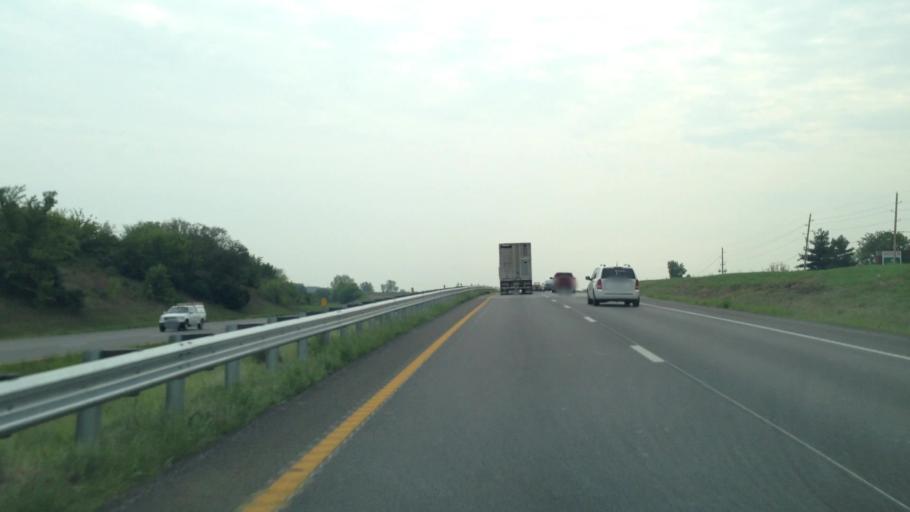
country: US
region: Missouri
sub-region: Clay County
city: Liberty
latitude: 39.2756
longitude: -94.4267
